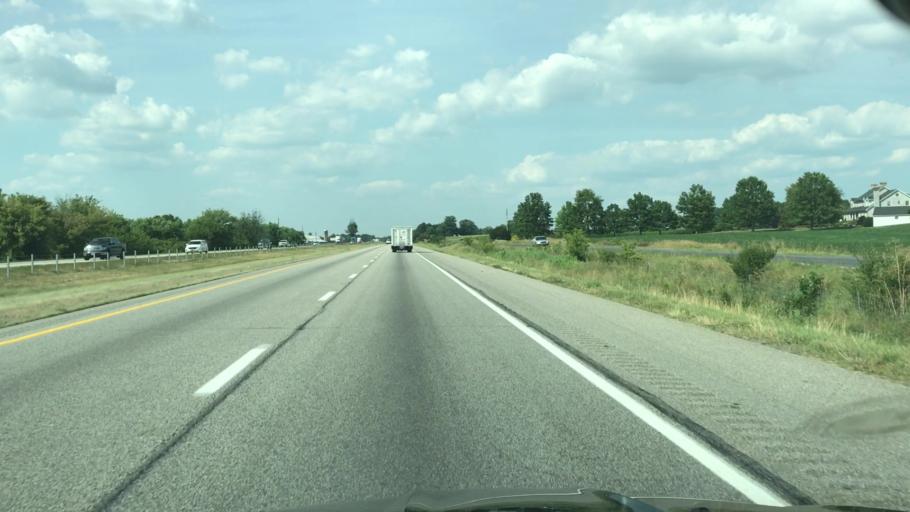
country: US
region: Pennsylvania
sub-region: Franklin County
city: Greencastle
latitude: 39.8341
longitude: -77.6961
